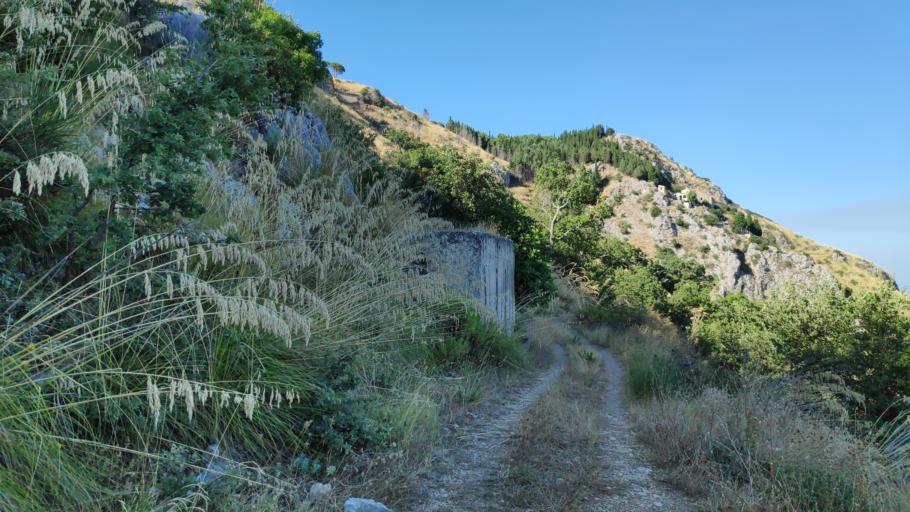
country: IT
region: Calabria
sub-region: Provincia di Reggio Calabria
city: Pazzano
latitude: 38.4660
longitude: 16.4458
